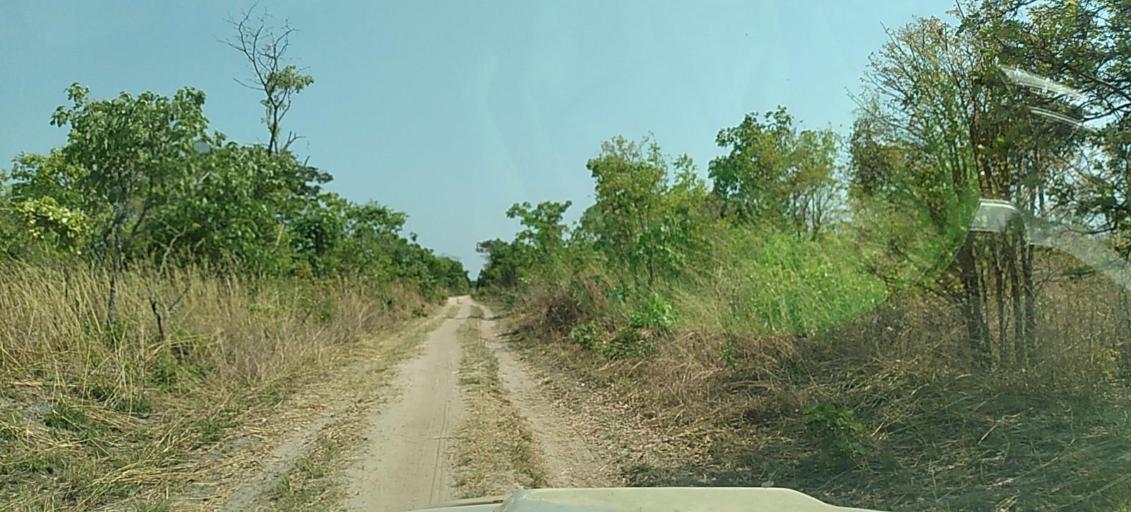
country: ZM
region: North-Western
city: Kalengwa
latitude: -13.2421
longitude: 24.7571
